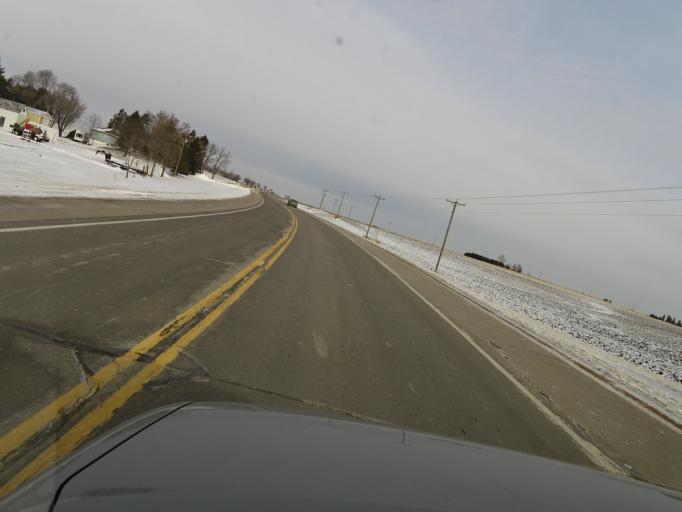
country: US
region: Minnesota
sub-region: Scott County
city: Jordan
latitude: 44.6765
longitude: -93.5723
